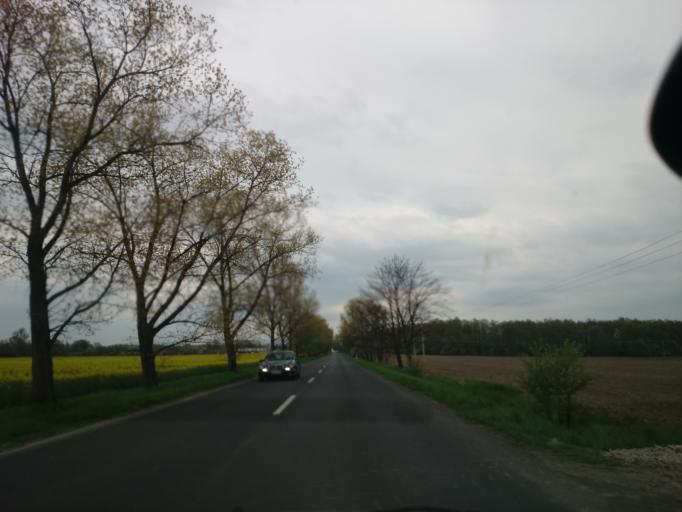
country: PL
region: Opole Voivodeship
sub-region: Powiat nyski
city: Nysa
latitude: 50.4425
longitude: 17.3424
